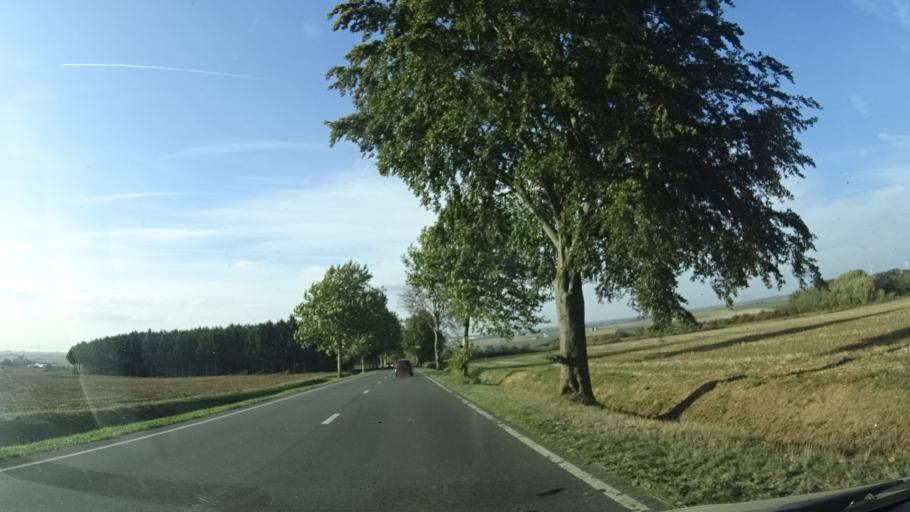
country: BE
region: Wallonia
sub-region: Province du Hainaut
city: Estinnes-au-Val
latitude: 50.3690
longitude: 4.0470
